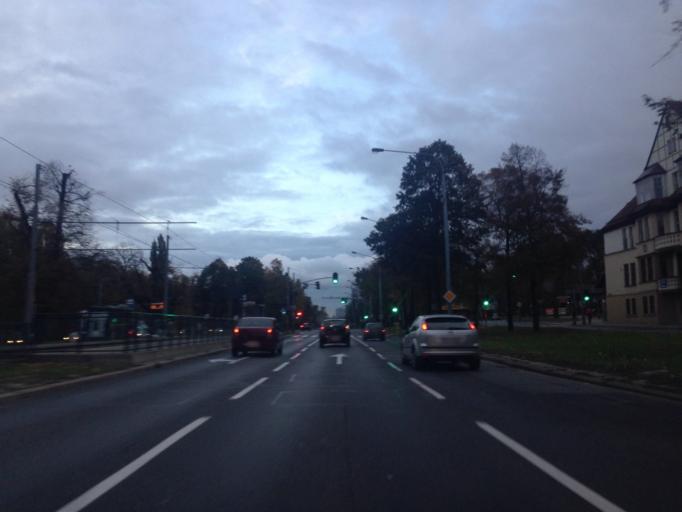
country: PL
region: Pomeranian Voivodeship
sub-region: Gdansk
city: Gdansk
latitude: 54.3694
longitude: 18.6289
